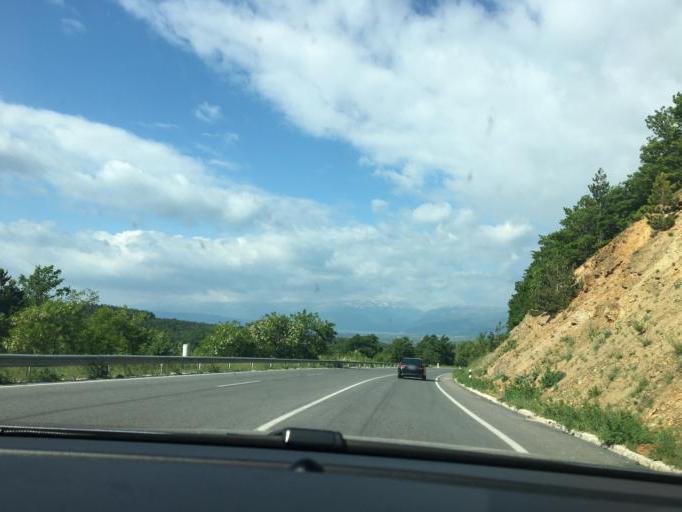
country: MK
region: Resen
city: Grncari
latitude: 41.0695
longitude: 21.0798
